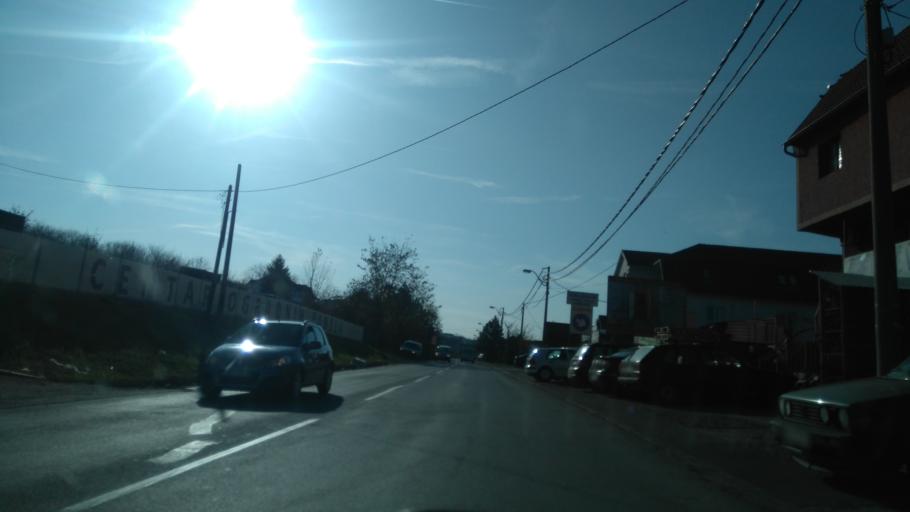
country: RS
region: Central Serbia
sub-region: Belgrade
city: Rakovica
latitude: 44.7401
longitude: 20.3885
